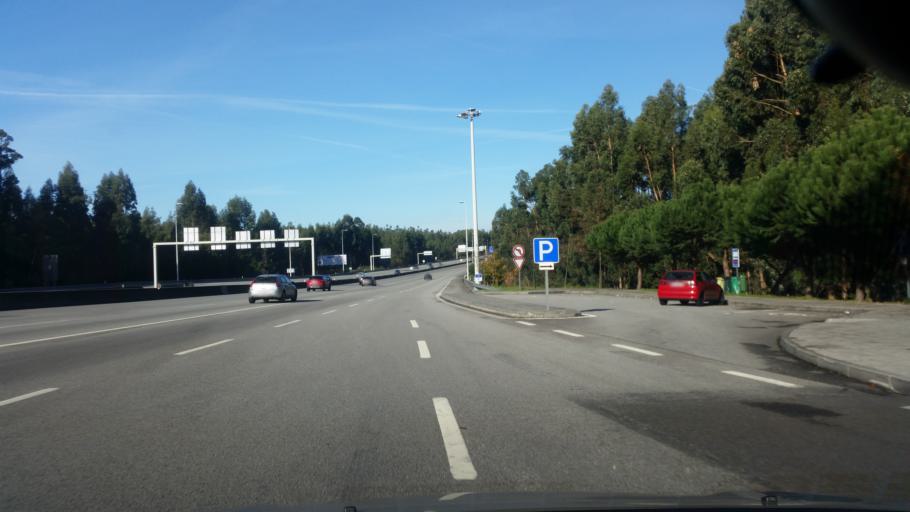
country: PT
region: Porto
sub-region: Maia
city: Nogueira
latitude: 41.2461
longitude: -8.5659
